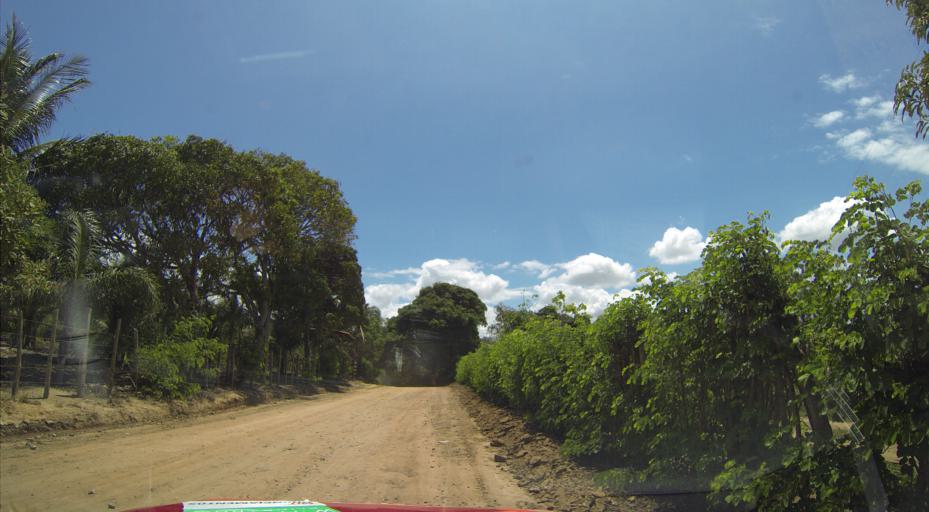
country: BR
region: Espirito Santo
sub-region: Serra
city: Serra
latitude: -20.0609
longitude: -40.2664
